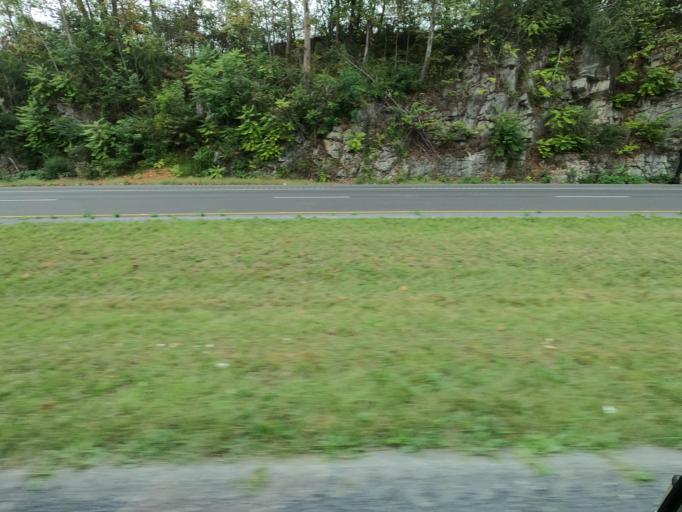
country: US
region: Tennessee
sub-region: Sullivan County
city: Colonial Heights
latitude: 36.5174
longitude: -82.5248
